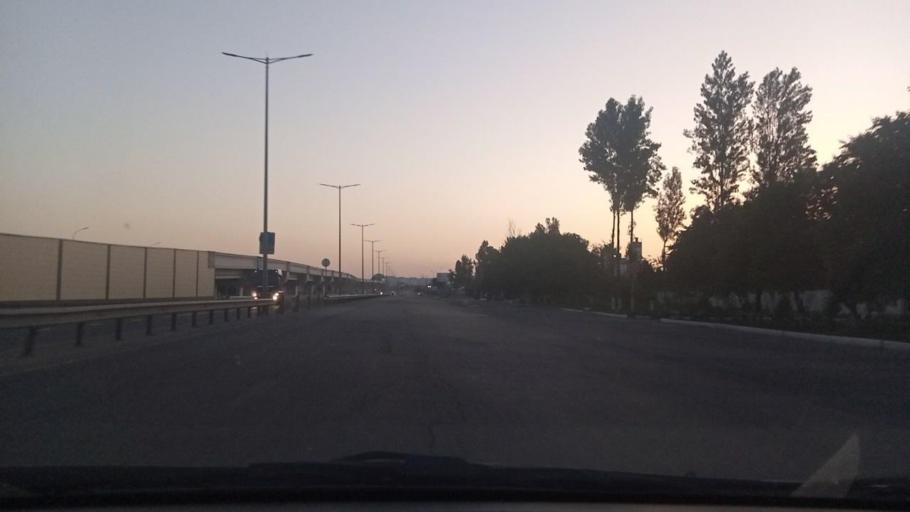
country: UZ
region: Toshkent Shahri
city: Bektemir
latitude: 41.2588
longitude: 69.3607
